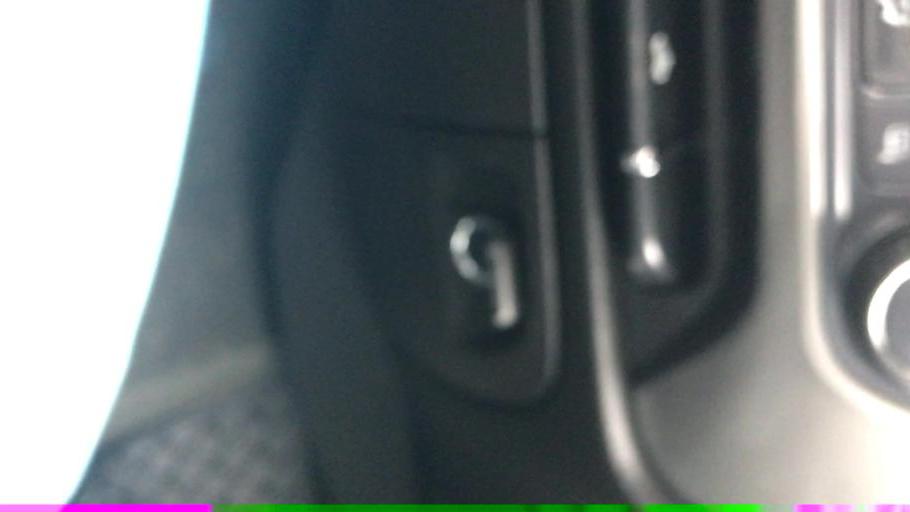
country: US
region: Texas
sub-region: Denton County
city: Flower Mound
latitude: 32.9952
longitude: -97.0642
